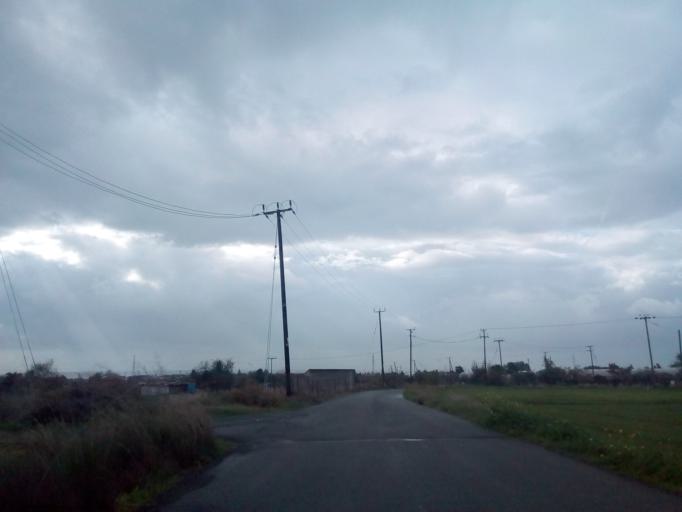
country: CY
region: Limassol
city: Ypsonas
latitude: 34.6731
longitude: 32.9646
